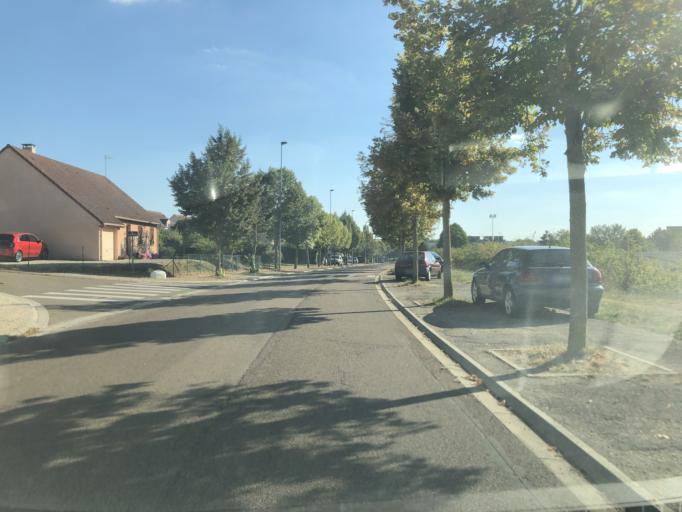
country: FR
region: Bourgogne
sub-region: Departement de l'Yonne
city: Auxerre
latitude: 47.8036
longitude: 3.5910
